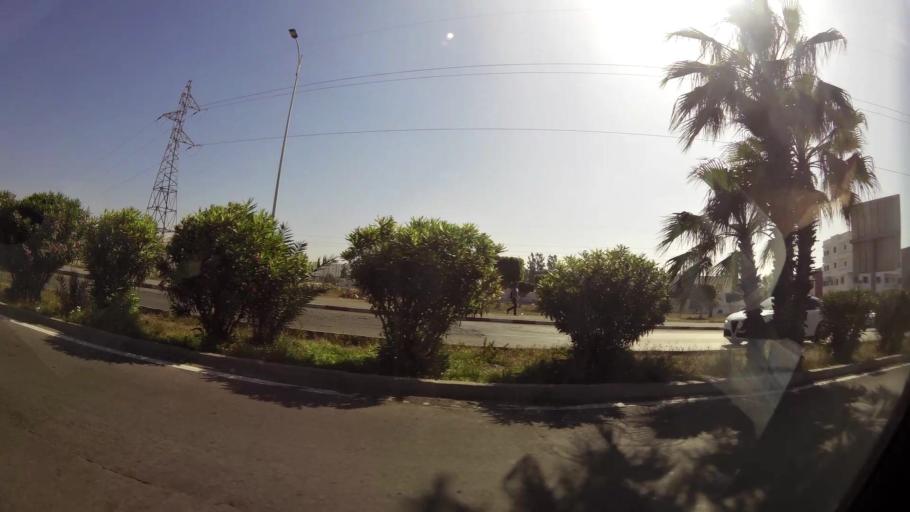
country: MA
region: Souss-Massa-Draa
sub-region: Inezgane-Ait Mellou
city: Inezgane
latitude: 30.3829
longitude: -9.5053
